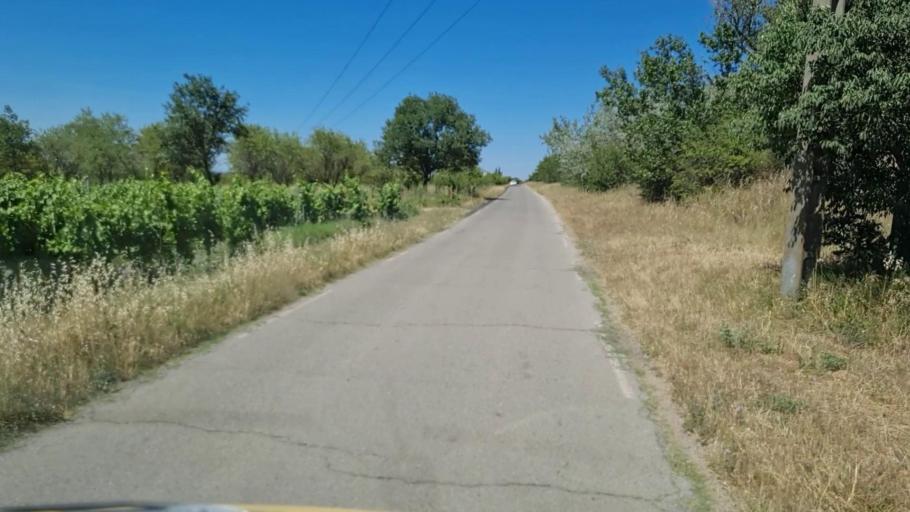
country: FR
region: Languedoc-Roussillon
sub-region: Departement du Gard
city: Vauvert
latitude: 43.6717
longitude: 4.2636
